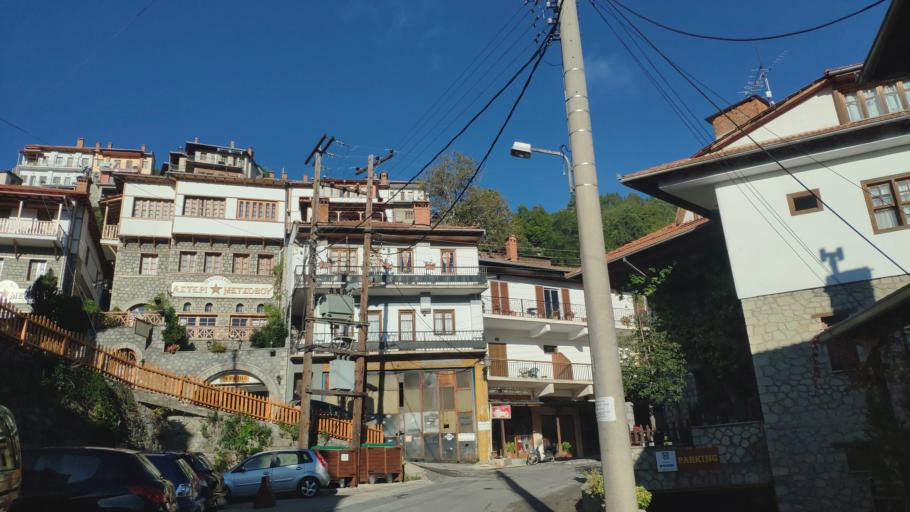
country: GR
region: Epirus
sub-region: Nomos Ioanninon
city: Metsovo
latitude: 39.7729
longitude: 21.1803
